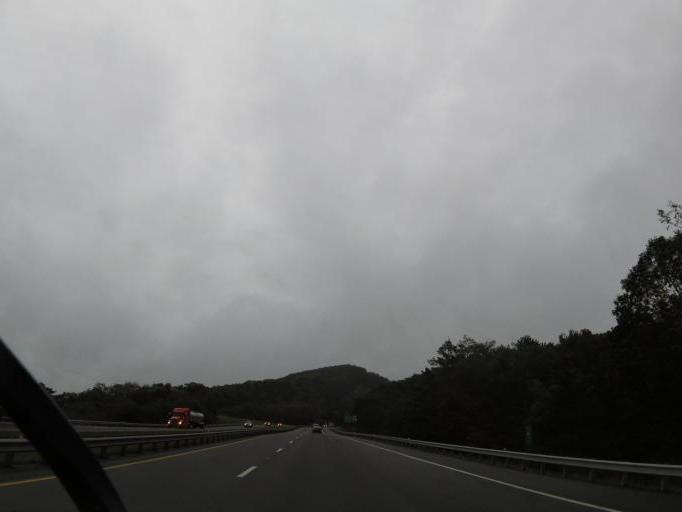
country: US
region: Virginia
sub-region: Bland County
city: Bland
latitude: 37.0289
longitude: -81.1138
